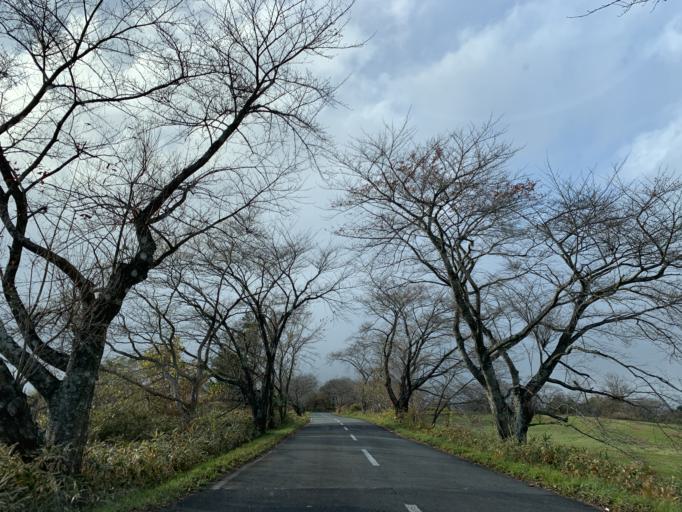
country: JP
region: Iwate
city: Mizusawa
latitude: 39.0388
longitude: 141.0814
